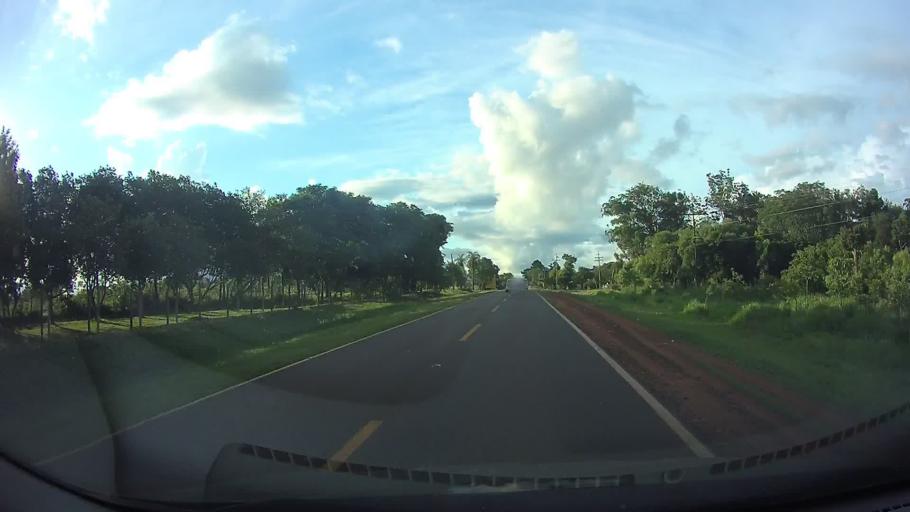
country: PY
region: Paraguari
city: Ybycui
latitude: -25.9951
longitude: -57.0516
